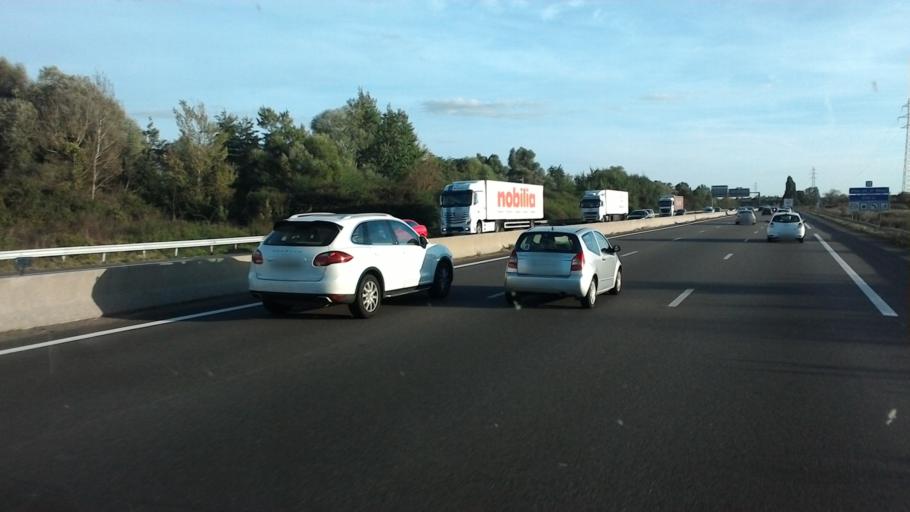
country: FR
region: Lorraine
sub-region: Departement de la Moselle
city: Maizieres-les-Metz
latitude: 49.1903
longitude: 6.1759
